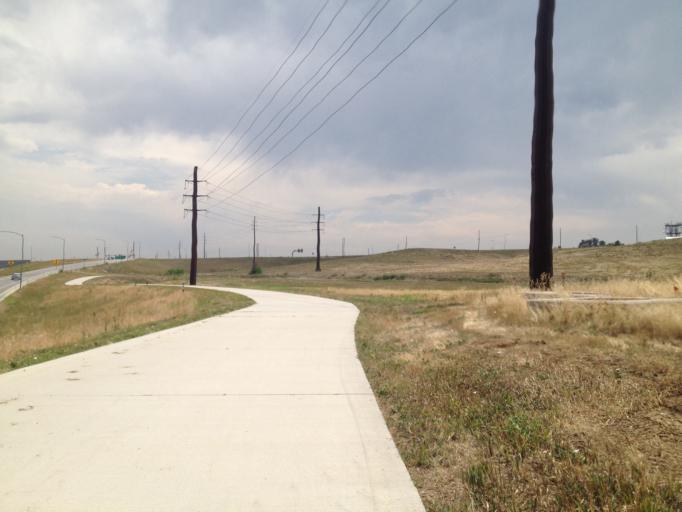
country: US
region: Colorado
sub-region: Broomfield County
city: Broomfield
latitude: 39.9186
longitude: -105.1000
